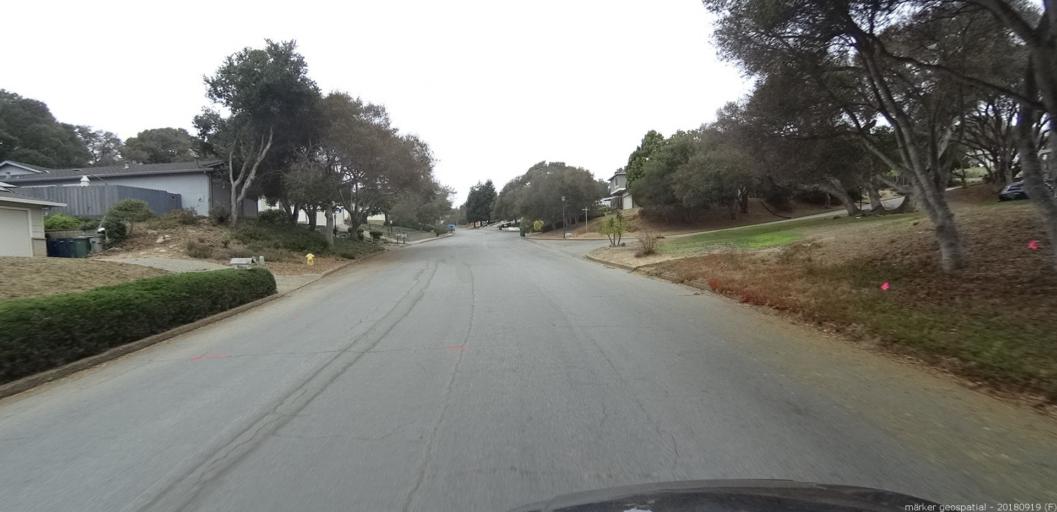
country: US
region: California
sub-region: Monterey County
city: Prunedale
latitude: 36.7809
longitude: -121.7140
